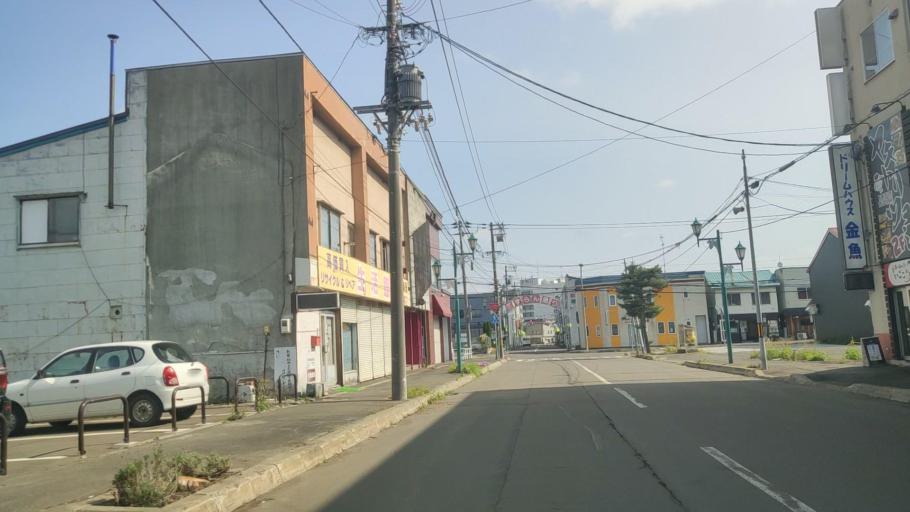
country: JP
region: Hokkaido
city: Shimo-furano
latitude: 43.3454
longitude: 142.3882
